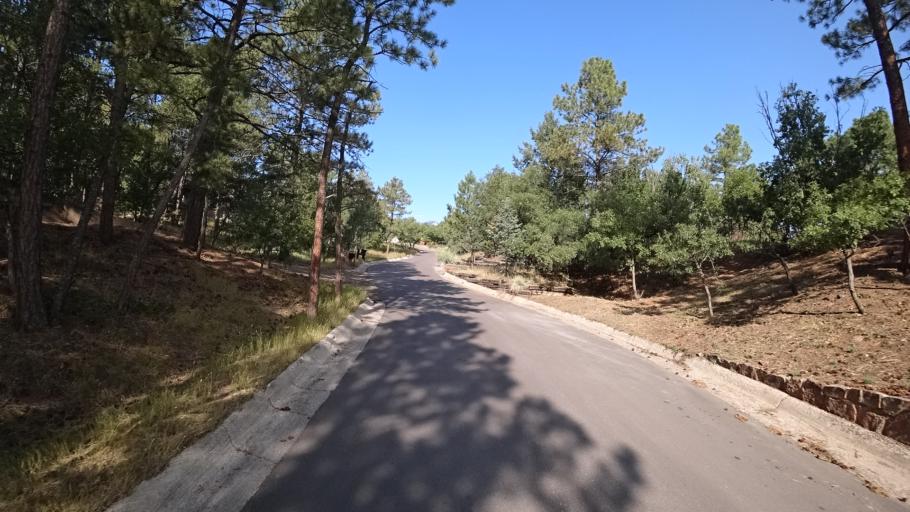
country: US
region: Colorado
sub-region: El Paso County
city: Colorado Springs
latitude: 38.8108
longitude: -104.8640
